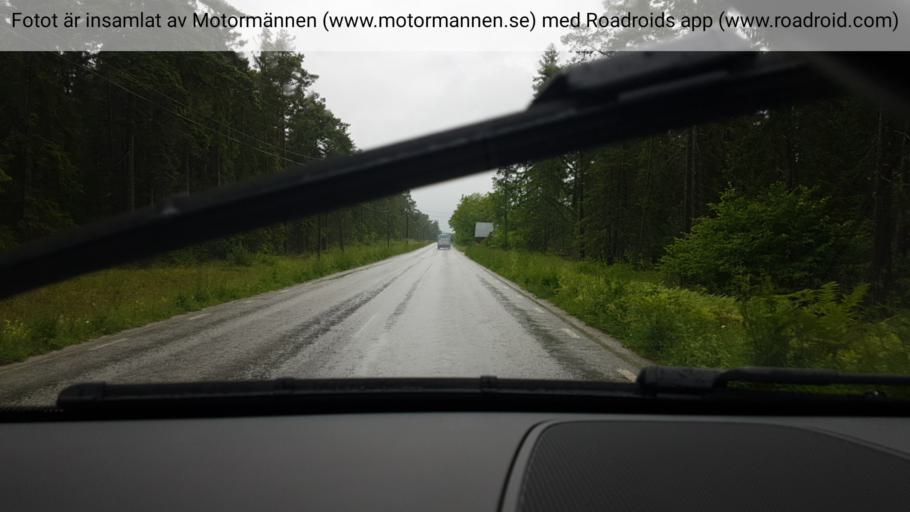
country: SE
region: Gotland
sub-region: Gotland
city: Slite
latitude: 57.6241
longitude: 18.7598
